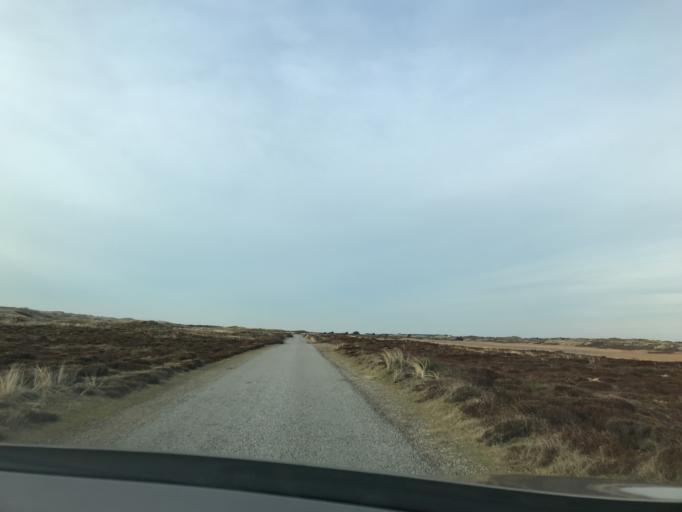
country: DK
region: South Denmark
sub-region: Varde Kommune
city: Oksbol
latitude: 55.7966
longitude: 8.1821
